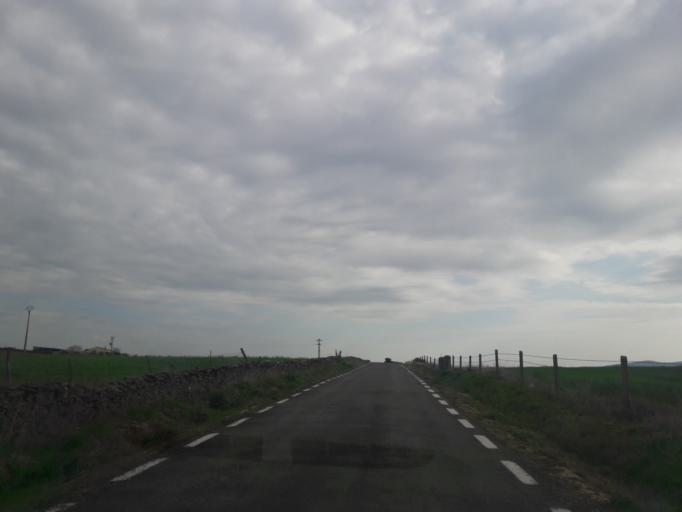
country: ES
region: Castille and Leon
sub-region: Provincia de Salamanca
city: Pastores
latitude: 40.5019
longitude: -6.5251
